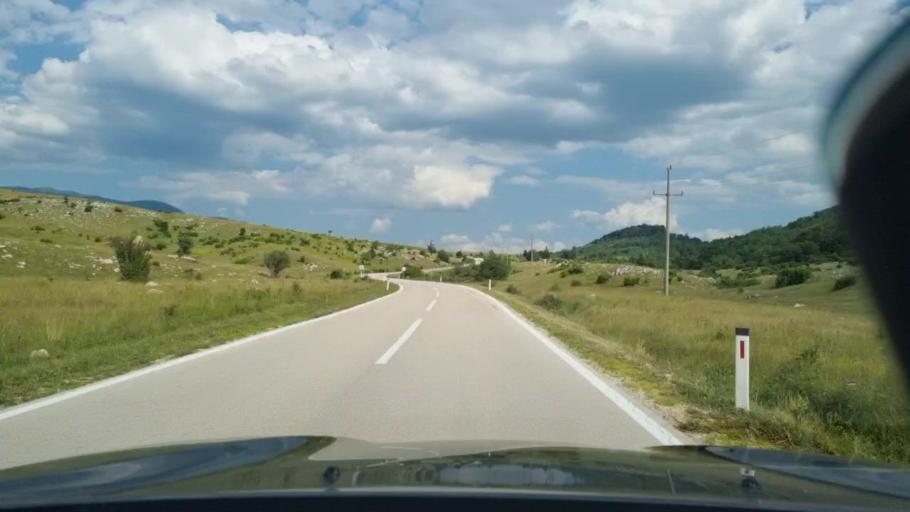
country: BA
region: Federation of Bosnia and Herzegovina
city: Bosansko Grahovo
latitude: 44.1311
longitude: 16.4891
